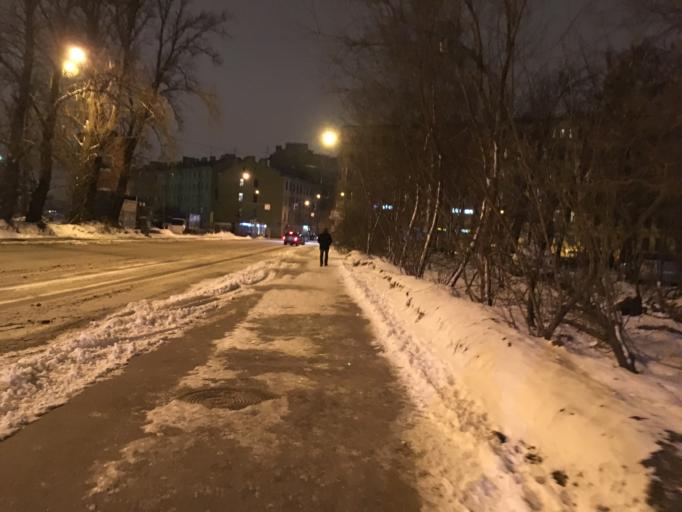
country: RU
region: St.-Petersburg
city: Centralniy
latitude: 59.9083
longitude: 30.3395
